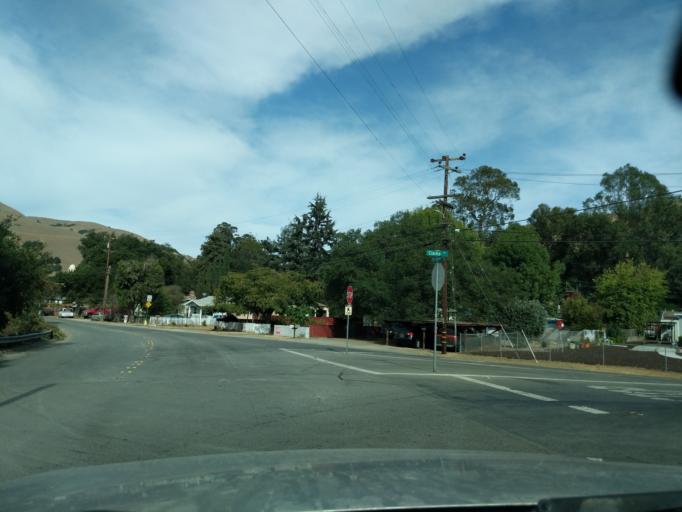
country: US
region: California
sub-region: Alameda County
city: Fremont
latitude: 37.5801
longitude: -121.9640
